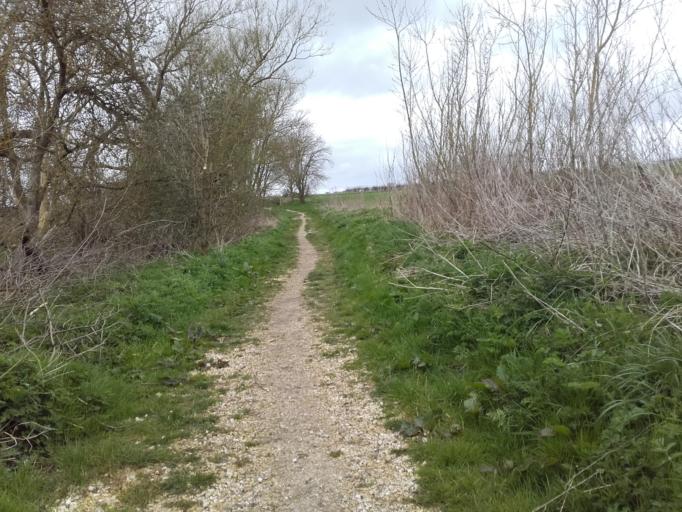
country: GB
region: England
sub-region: East Riding of Yorkshire
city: Market Weighton
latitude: 53.8810
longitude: -0.6534
